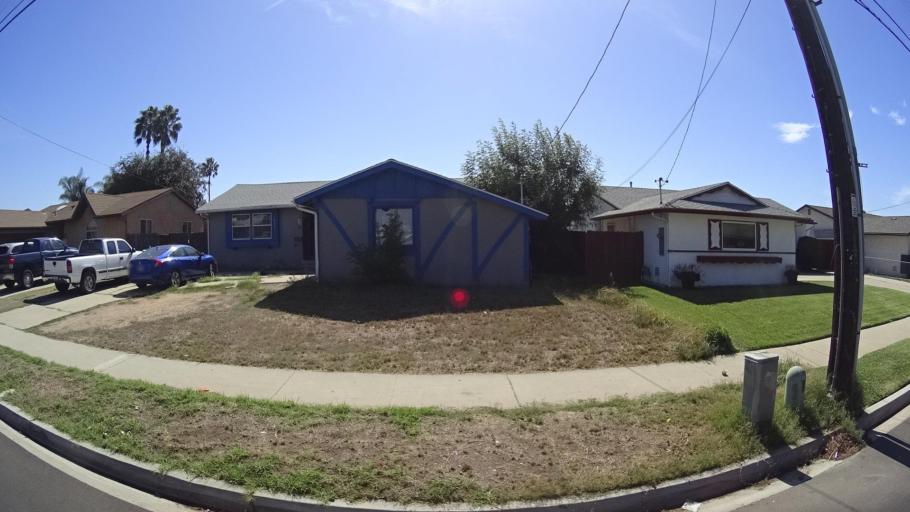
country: US
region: California
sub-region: San Diego County
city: La Presa
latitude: 32.7122
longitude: -117.0102
